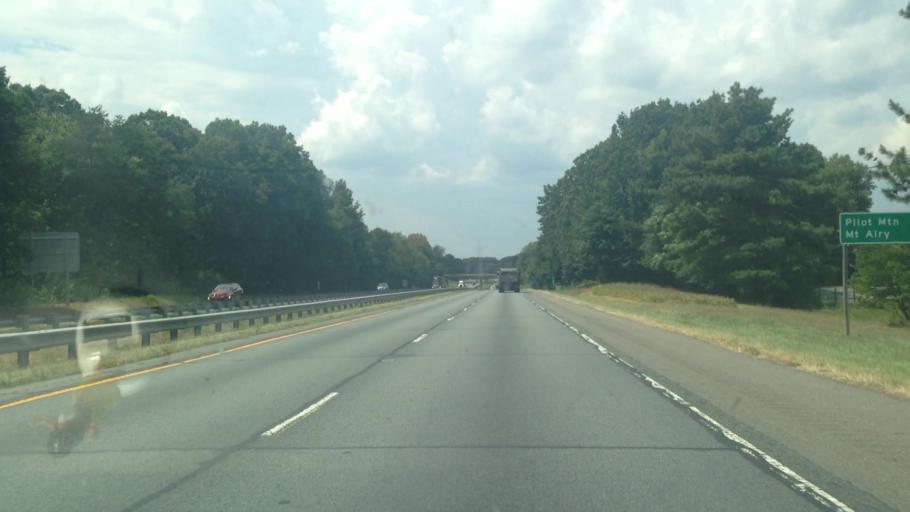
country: US
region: North Carolina
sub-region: Stokes County
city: King
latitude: 36.2691
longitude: -80.3736
